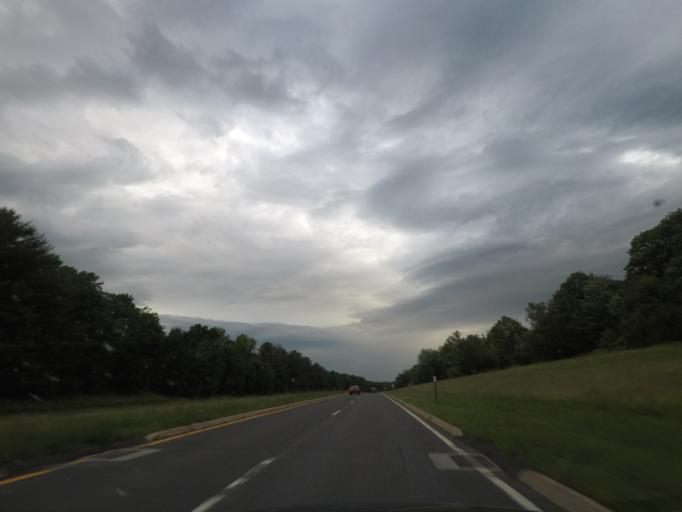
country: US
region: New York
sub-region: Columbia County
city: Philmont
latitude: 42.2221
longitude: -73.6320
